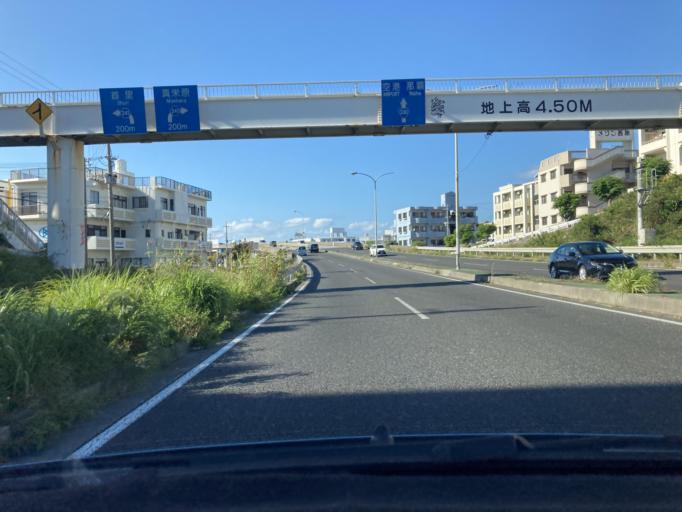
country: JP
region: Okinawa
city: Ginowan
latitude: 26.2520
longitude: 127.7408
